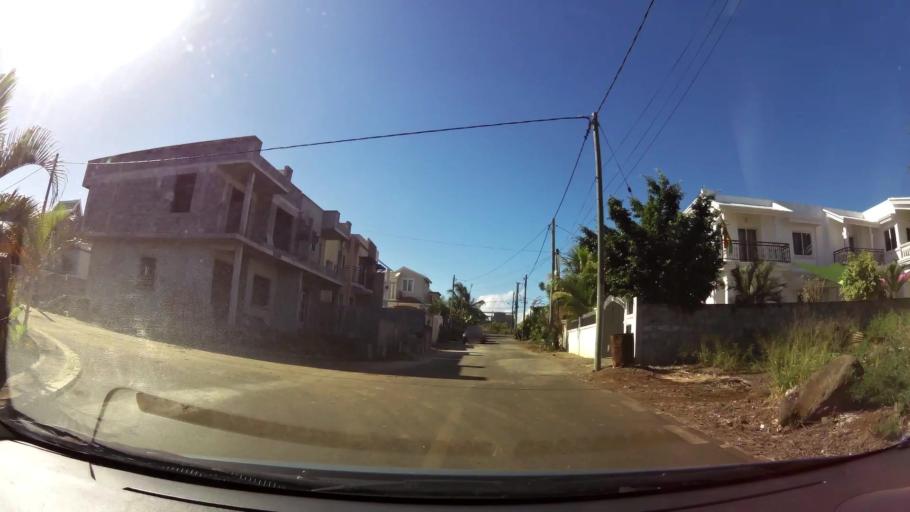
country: MU
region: Black River
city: Flic en Flac
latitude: -20.2778
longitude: 57.3792
